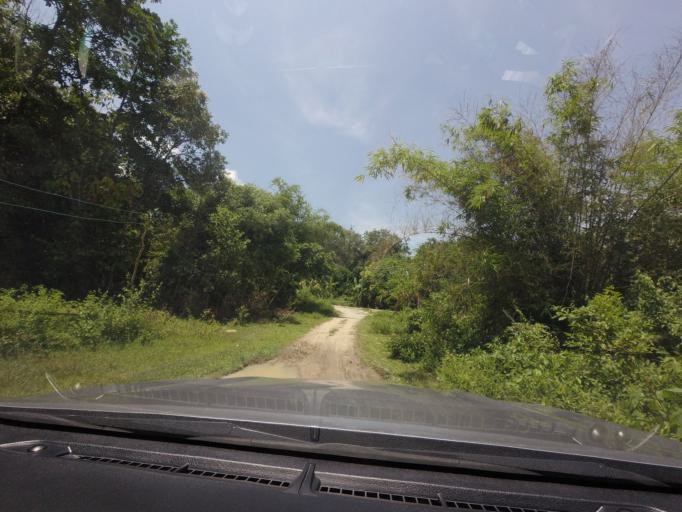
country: TH
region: Narathiwat
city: Rueso
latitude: 6.3825
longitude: 101.5146
